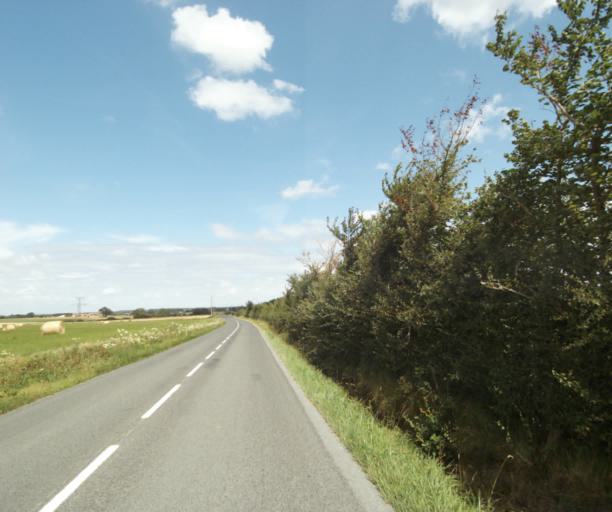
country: FR
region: Pays de la Loire
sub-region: Departement de la Sarthe
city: Auvers-le-Hamon
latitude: 47.8738
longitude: -0.3412
